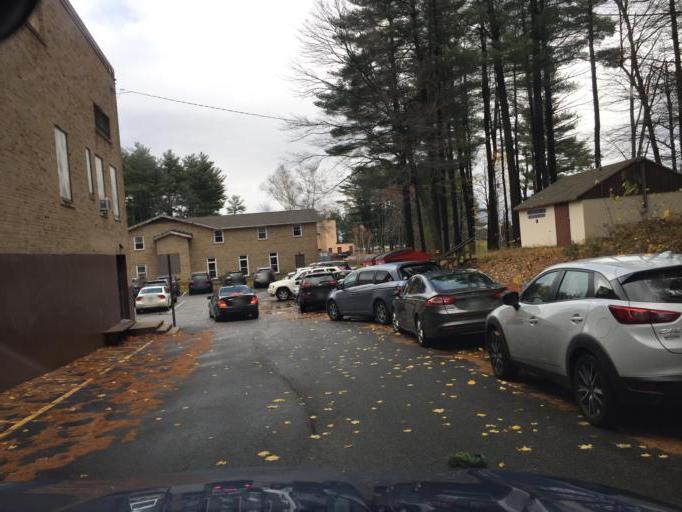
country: US
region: New Hampshire
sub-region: Hillsborough County
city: Manchester
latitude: 42.9949
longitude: -71.4377
